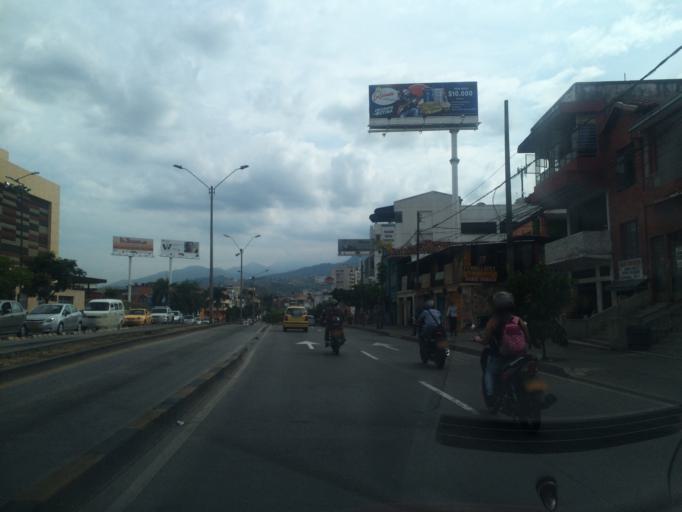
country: CO
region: Valle del Cauca
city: Cali
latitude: 3.4369
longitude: -76.5394
